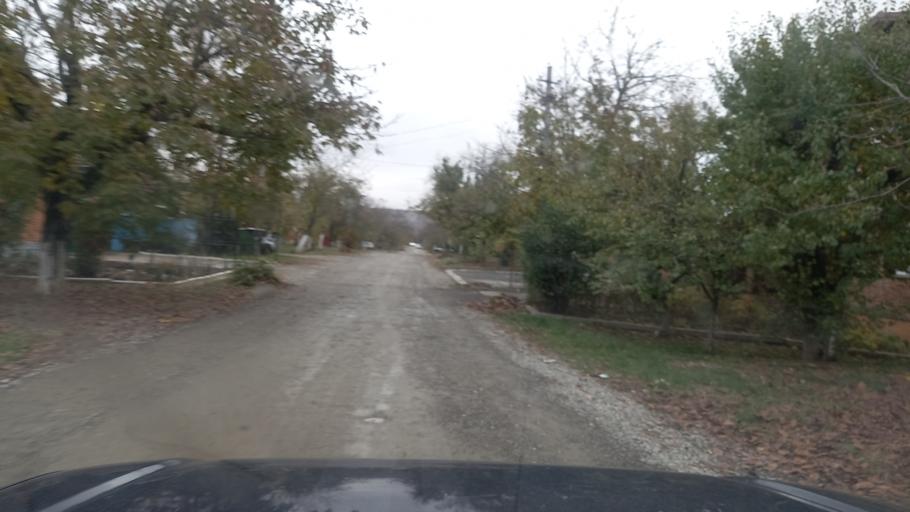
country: RU
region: Adygeya
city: Maykop
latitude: 44.6055
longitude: 40.0845
